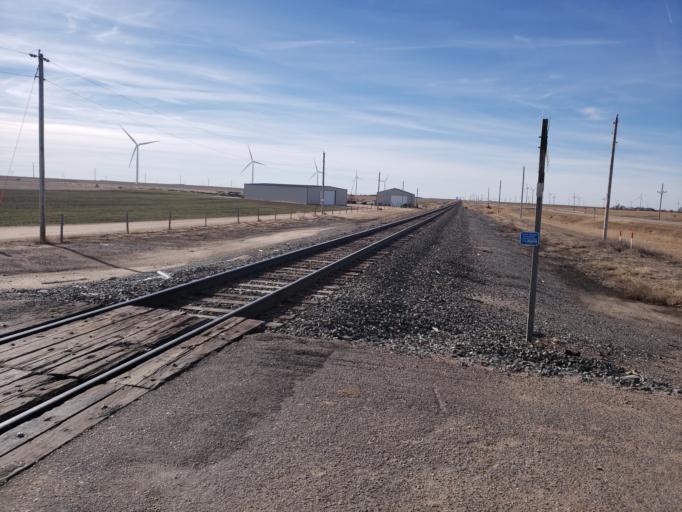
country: US
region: Kansas
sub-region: Ford County
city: Dodge City
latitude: 37.8262
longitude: -99.8062
